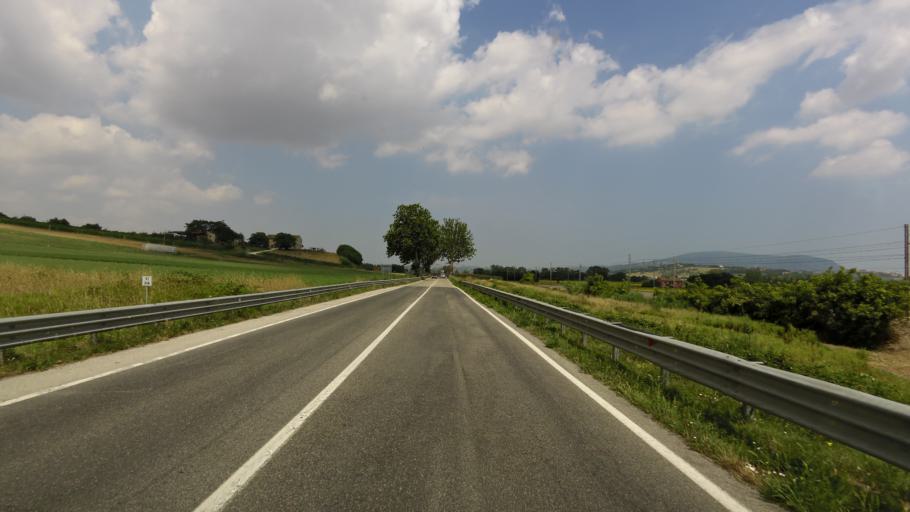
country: IT
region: The Marches
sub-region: Provincia di Ancona
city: Villa Musone
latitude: 43.4677
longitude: 13.6010
